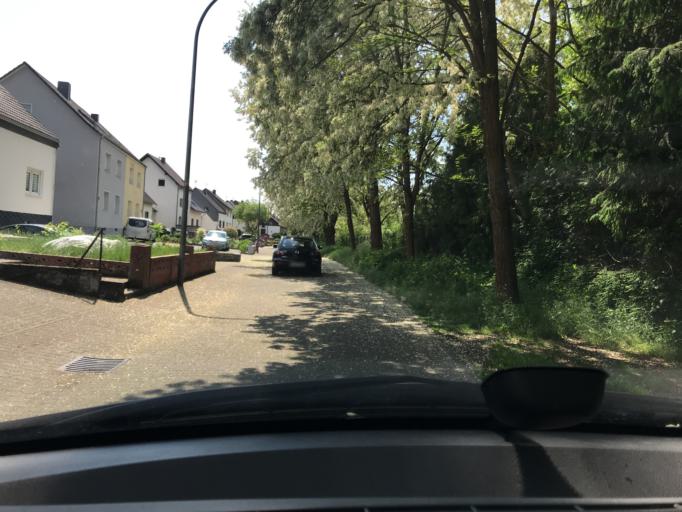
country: DE
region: Saarland
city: Saarlouis
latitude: 49.3343
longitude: 6.7599
